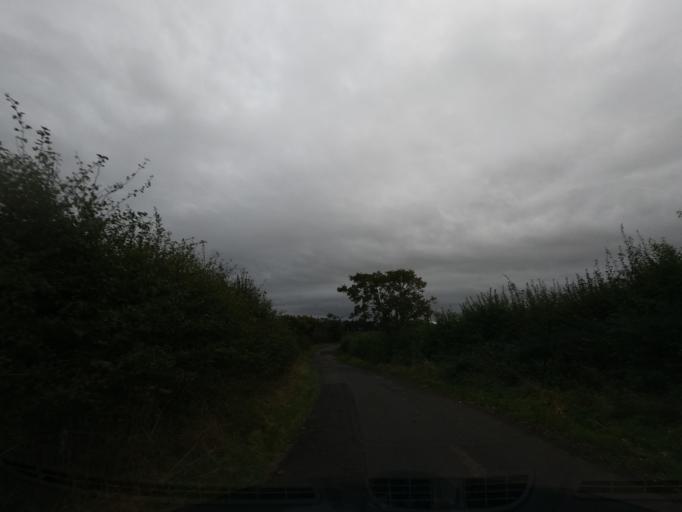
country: GB
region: England
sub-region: Northumberland
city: Ford
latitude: 55.7033
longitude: -2.0866
